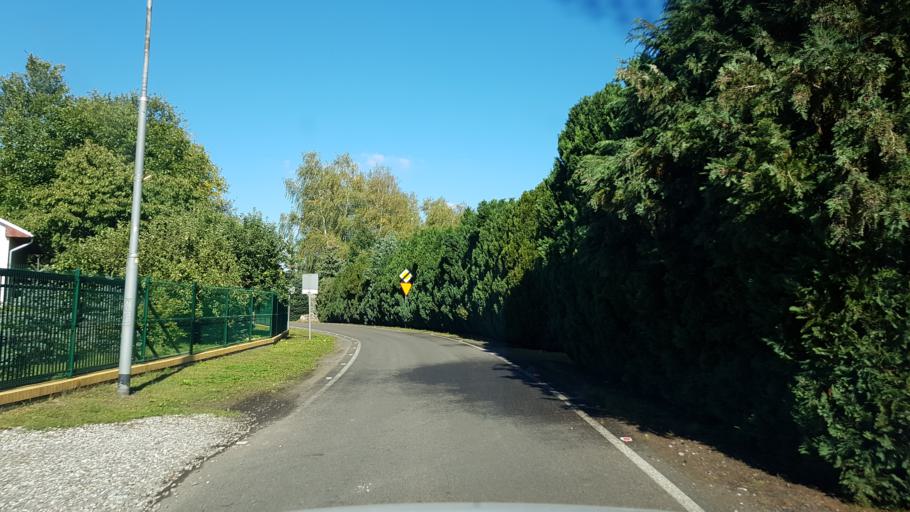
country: PL
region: West Pomeranian Voivodeship
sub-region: Powiat mysliborski
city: Nowogrodek Pomorski
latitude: 52.8655
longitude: 14.9688
